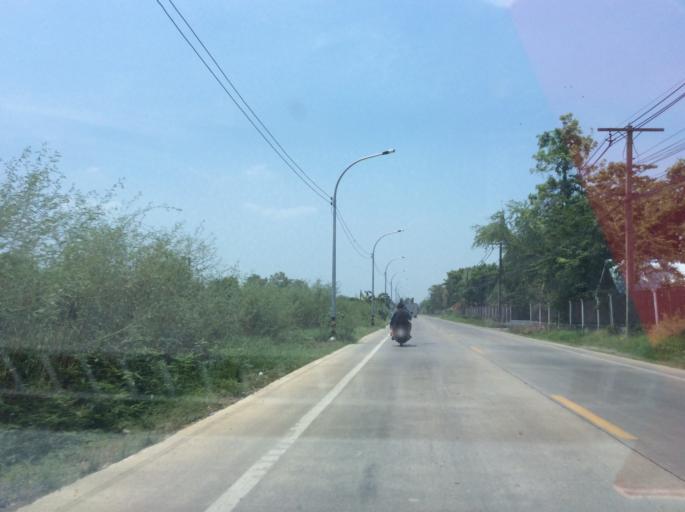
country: TH
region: Pathum Thani
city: Ban Rangsit
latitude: 14.0299
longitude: 100.7787
